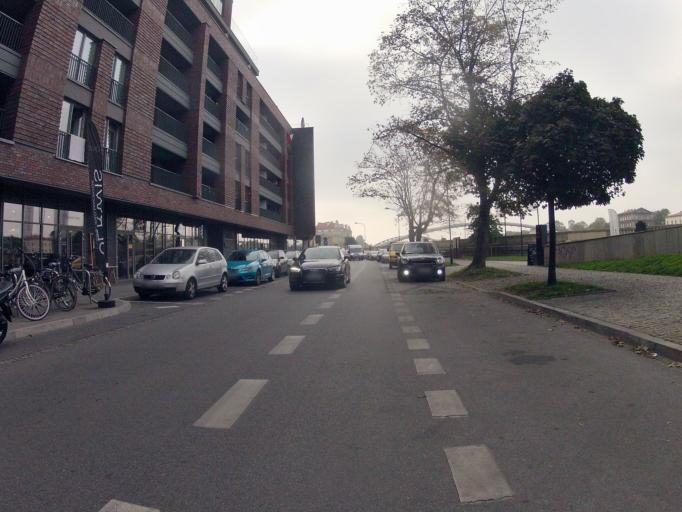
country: PL
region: Lesser Poland Voivodeship
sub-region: Krakow
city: Krakow
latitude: 50.0471
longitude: 19.9511
